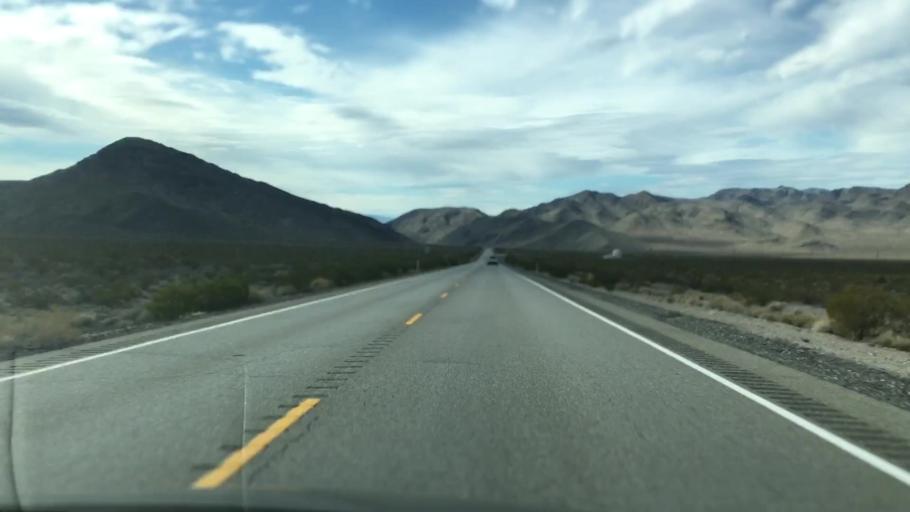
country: US
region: Nevada
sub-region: Nye County
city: Pahrump
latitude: 36.5921
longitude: -116.0292
